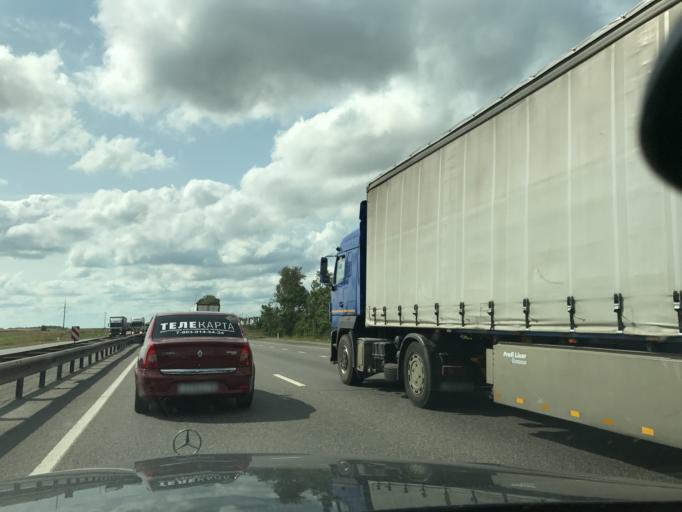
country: RU
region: Vladimir
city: Gorokhovets
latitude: 56.1693
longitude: 42.6340
